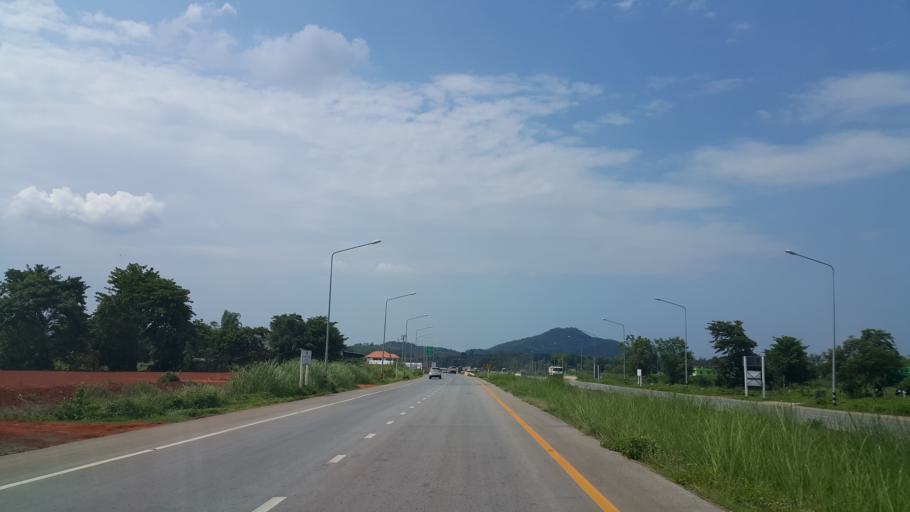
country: TH
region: Chiang Rai
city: Chiang Rai
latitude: 20.0008
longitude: 99.8928
